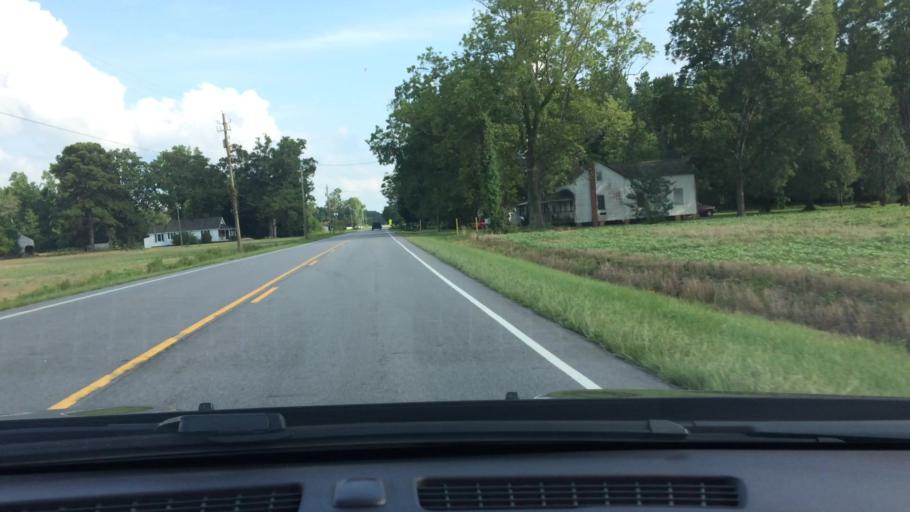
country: US
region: North Carolina
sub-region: Beaufort County
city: River Road
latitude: 35.4526
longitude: -77.0569
